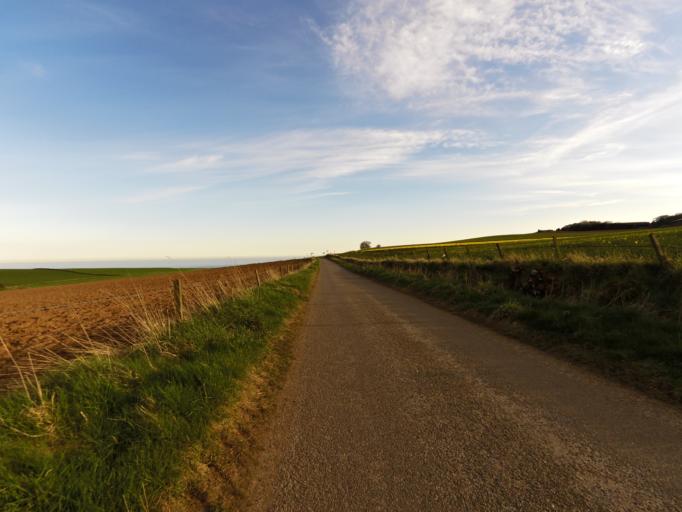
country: GB
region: Scotland
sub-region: Aberdeenshire
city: Inverbervie
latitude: 56.8798
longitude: -2.2358
